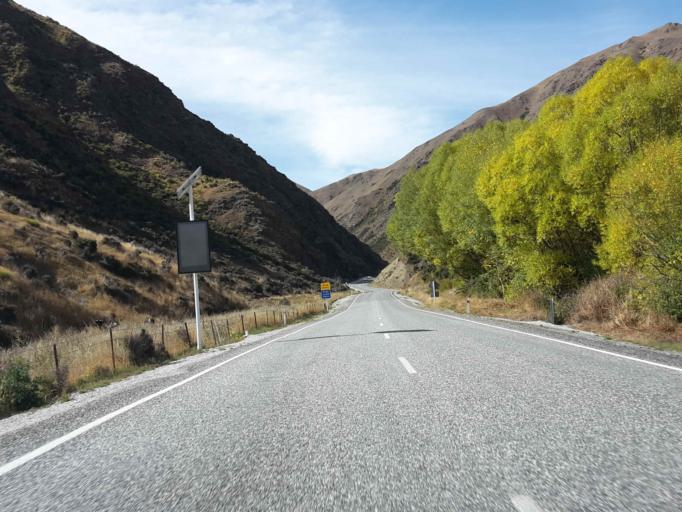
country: NZ
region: Otago
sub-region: Queenstown-Lakes District
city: Wanaka
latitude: -44.5999
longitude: 169.5565
